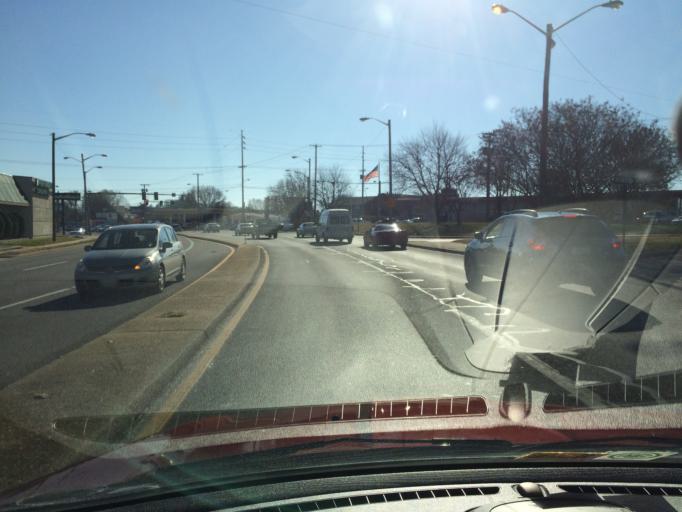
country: US
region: Virginia
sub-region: Roanoke County
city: Hollins
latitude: 37.3176
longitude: -79.9555
